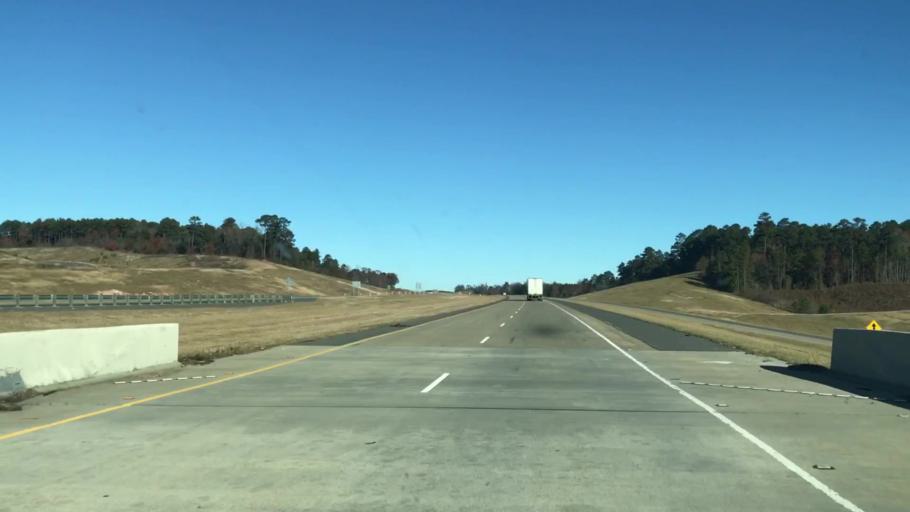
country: US
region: Louisiana
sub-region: Caddo Parish
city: Vivian
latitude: 32.9439
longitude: -93.8977
